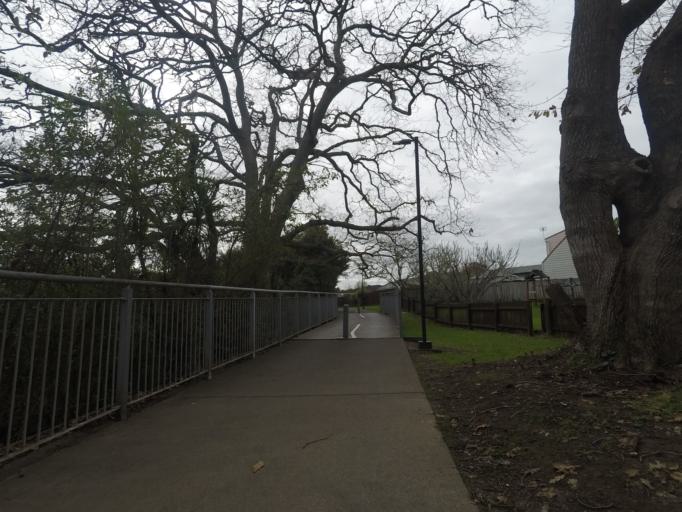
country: NZ
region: Auckland
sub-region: Auckland
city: Waitakere
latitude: -36.8960
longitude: 174.6318
